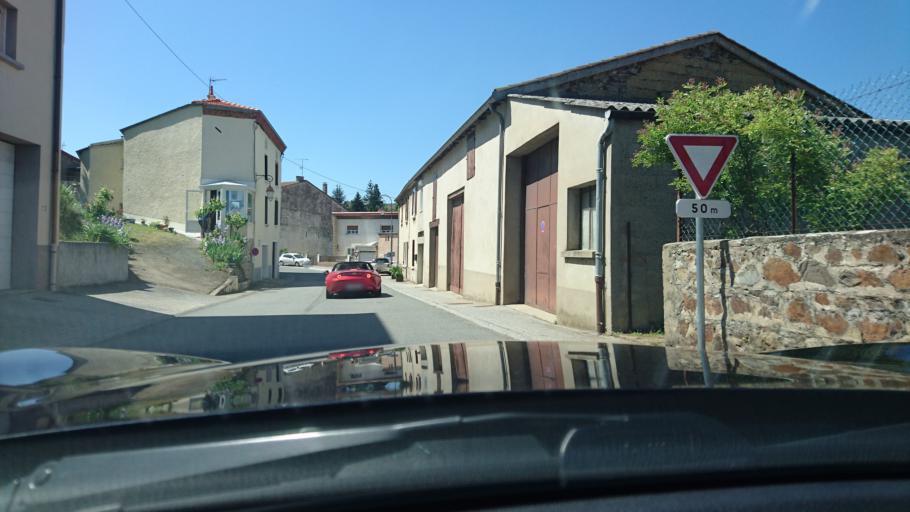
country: FR
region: Rhone-Alpes
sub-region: Departement de la Loire
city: Saint-Just-la-Pendue
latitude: 45.8792
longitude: 4.2754
